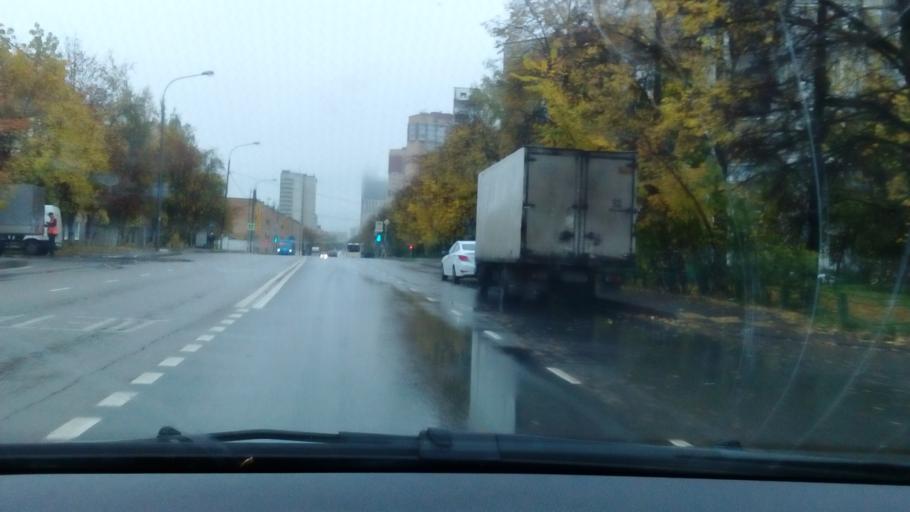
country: RU
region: Moskovskaya
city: Levoberezhnaya
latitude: 55.8729
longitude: 37.4693
